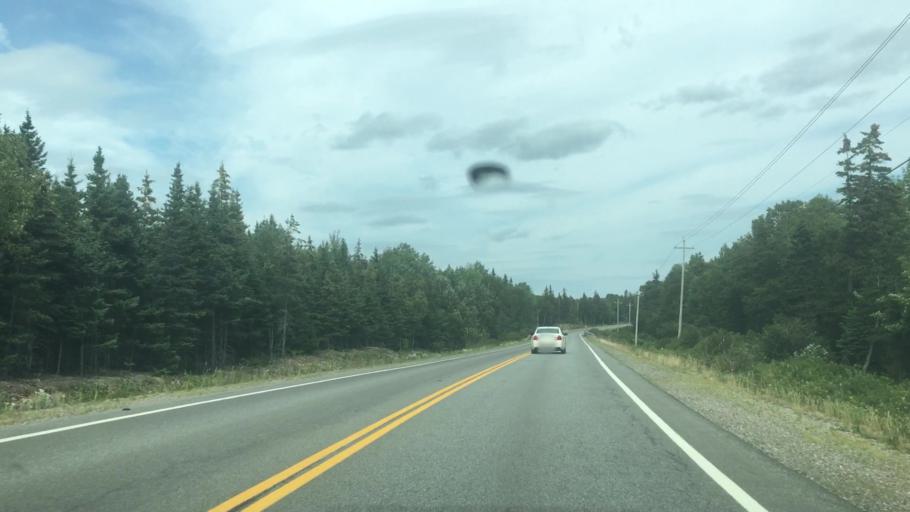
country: CA
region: Nova Scotia
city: Sydney Mines
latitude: 46.5119
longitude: -60.4305
